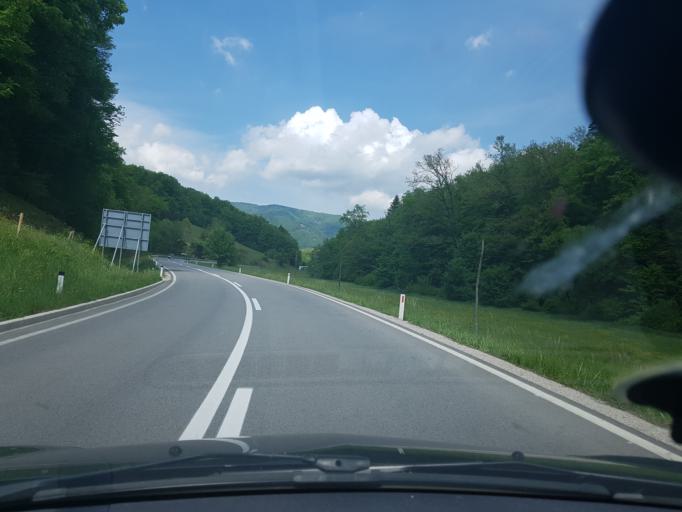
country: SI
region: Rogatec
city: Rogatec
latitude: 46.2301
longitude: 15.6747
